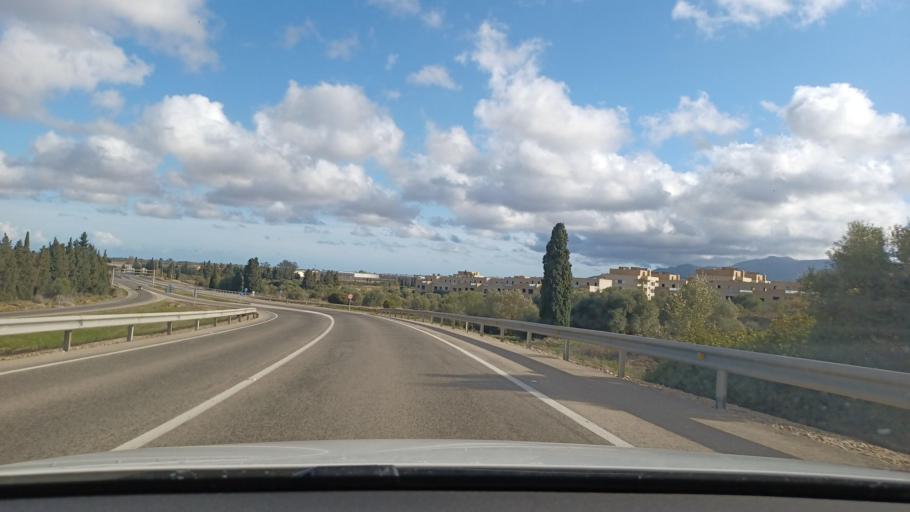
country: ES
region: Catalonia
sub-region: Provincia de Tarragona
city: Amposta
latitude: 40.7310
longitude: 0.5850
